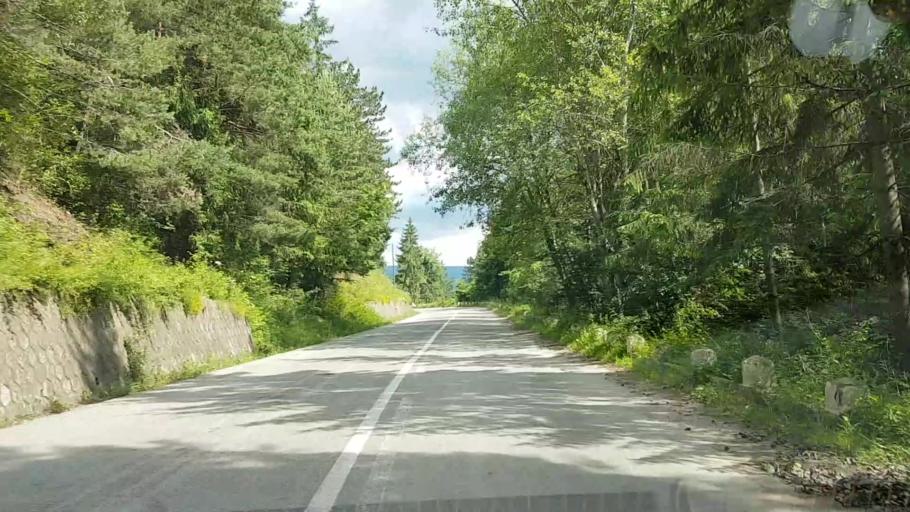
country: RO
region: Neamt
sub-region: Comuna Hangu
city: Hangu
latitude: 47.0485
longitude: 26.0125
